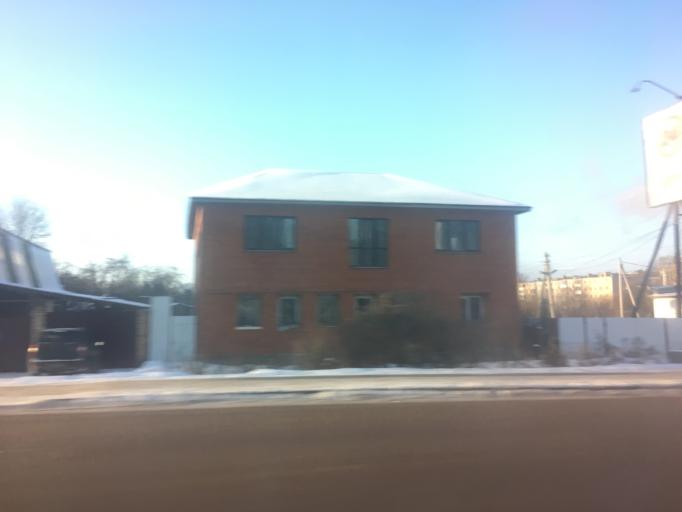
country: RU
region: Tula
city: Tula
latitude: 54.2033
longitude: 37.6794
